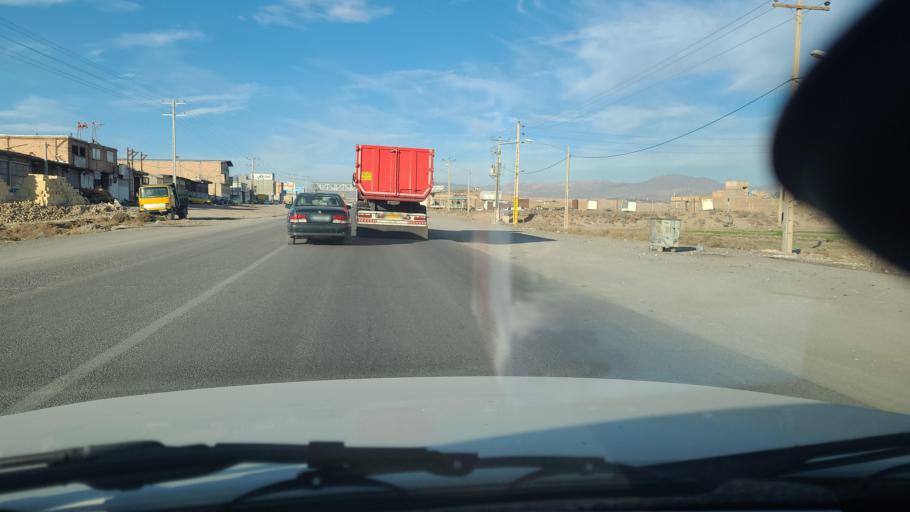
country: IR
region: Razavi Khorasan
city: Sabzevar
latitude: 36.2192
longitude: 57.6514
